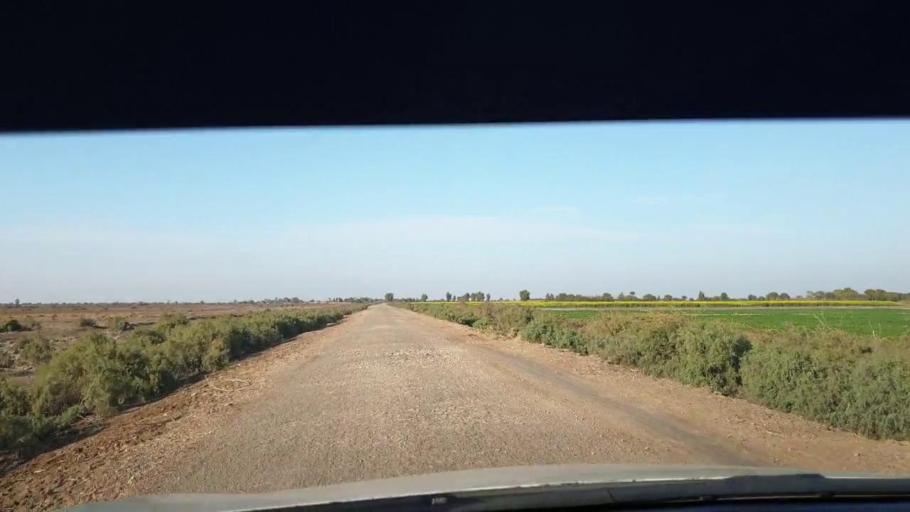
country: PK
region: Sindh
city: Berani
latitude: 25.8125
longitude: 68.9101
